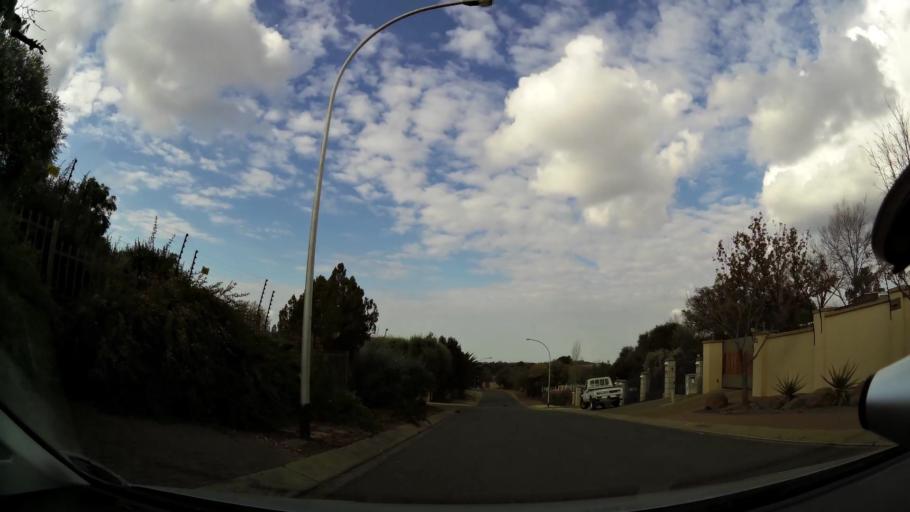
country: ZA
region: Orange Free State
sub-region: Mangaung Metropolitan Municipality
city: Bloemfontein
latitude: -29.0803
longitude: 26.2033
